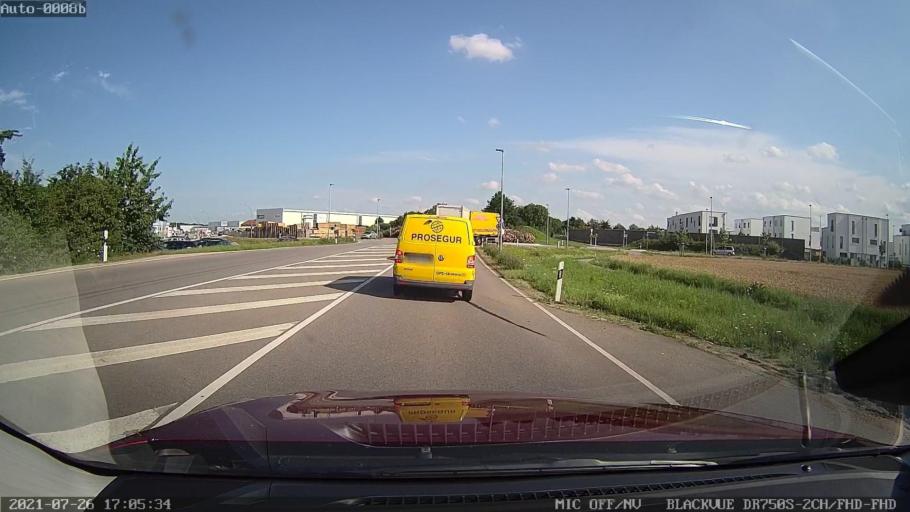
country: DE
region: Bavaria
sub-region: Upper Palatinate
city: Neutraubling
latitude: 48.9924
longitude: 12.2156
